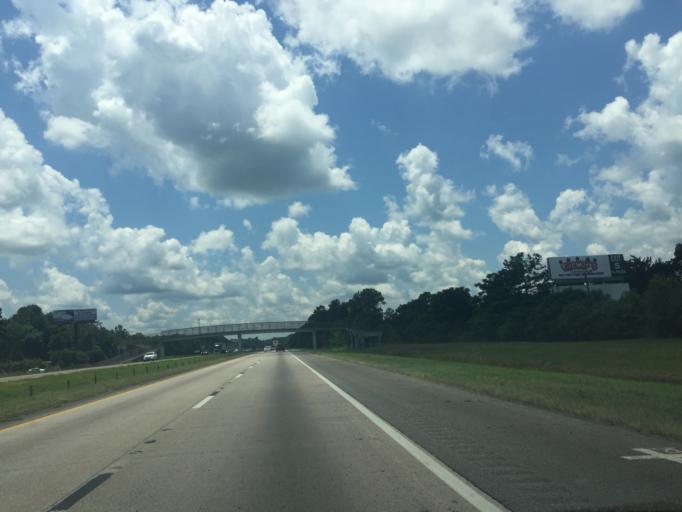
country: US
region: South Carolina
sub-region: Jasper County
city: Ridgeland
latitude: 32.4609
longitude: -80.9818
